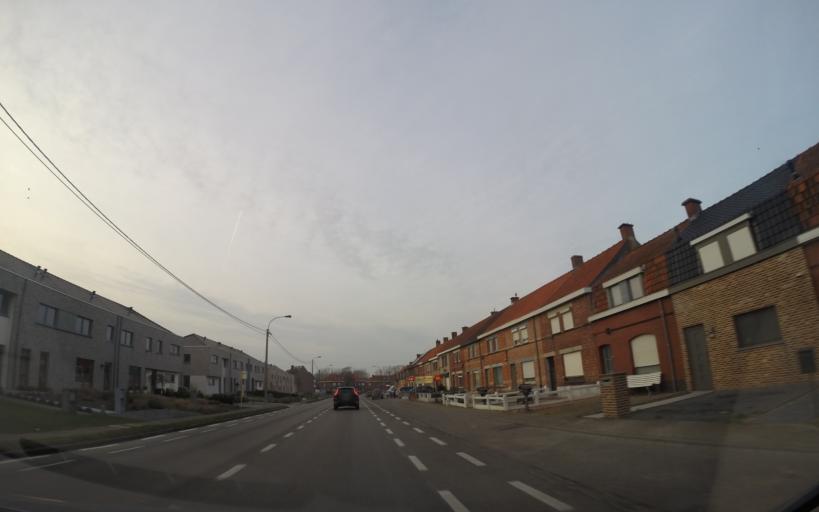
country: BE
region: Flanders
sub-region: Provincie Oost-Vlaanderen
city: Deinze
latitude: 50.9915
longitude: 3.5044
